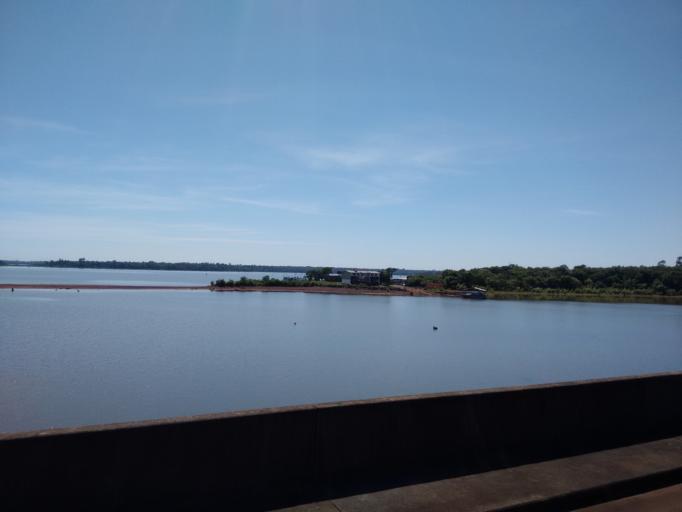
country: PY
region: Alto Parana
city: Ciudad del Este
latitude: -25.4357
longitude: -54.5619
